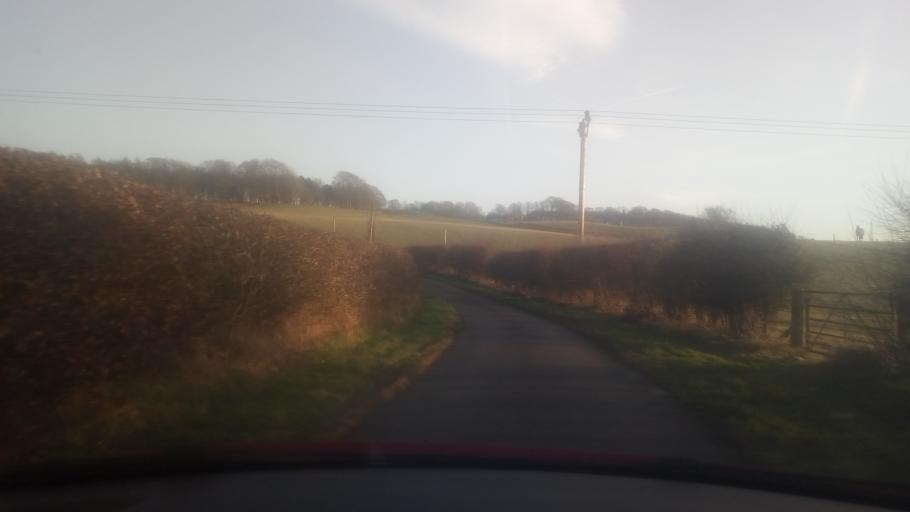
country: GB
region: Scotland
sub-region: The Scottish Borders
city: Jedburgh
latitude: 55.5049
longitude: -2.5372
